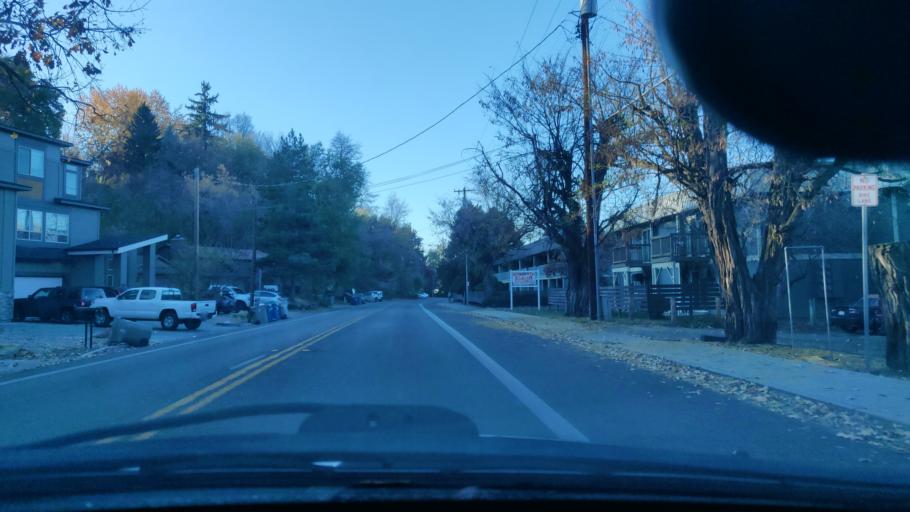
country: US
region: Idaho
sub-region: Ada County
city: Boise
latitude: 43.6014
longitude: -116.2096
